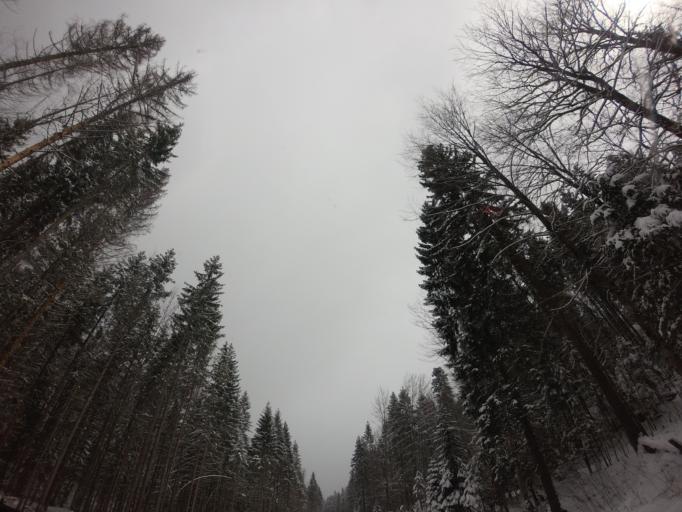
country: DE
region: Bavaria
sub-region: Upper Bavaria
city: Grainau
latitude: 47.4814
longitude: 11.0163
